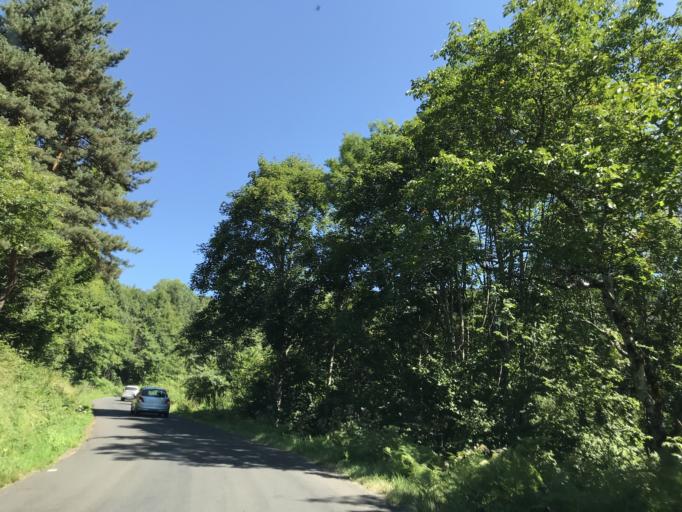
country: FR
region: Auvergne
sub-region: Departement du Puy-de-Dome
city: Job
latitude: 45.6699
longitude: 3.7296
